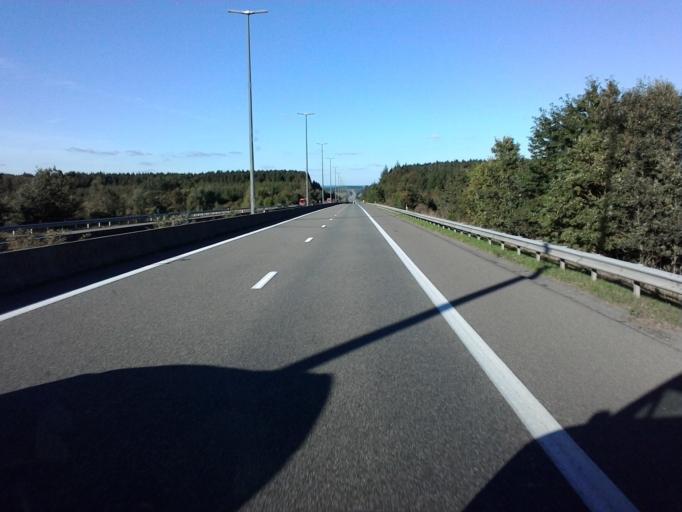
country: BE
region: Wallonia
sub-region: Province du Luxembourg
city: Bastogne
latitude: 50.0615
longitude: 5.7268
